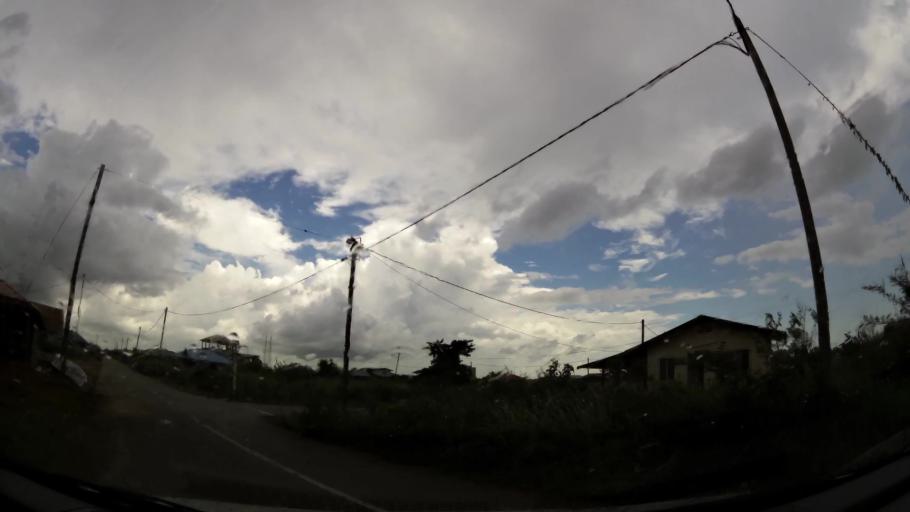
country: SR
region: Commewijne
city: Nieuw Amsterdam
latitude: 5.8538
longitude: -55.1128
